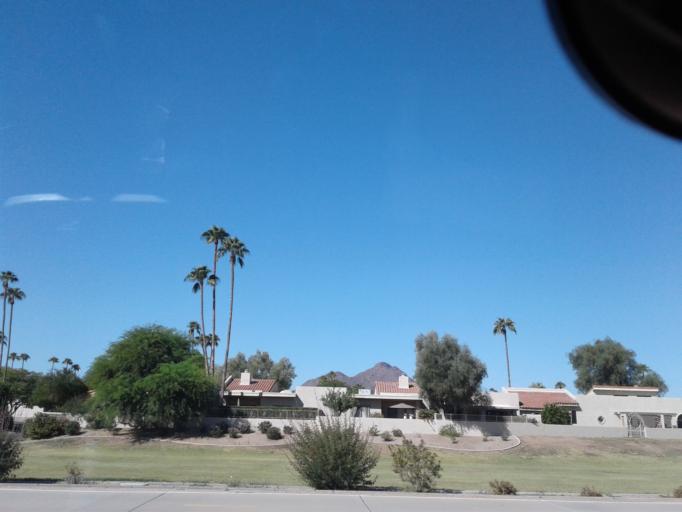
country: US
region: Arizona
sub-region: Maricopa County
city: Scottsdale
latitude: 33.5126
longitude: -111.9089
